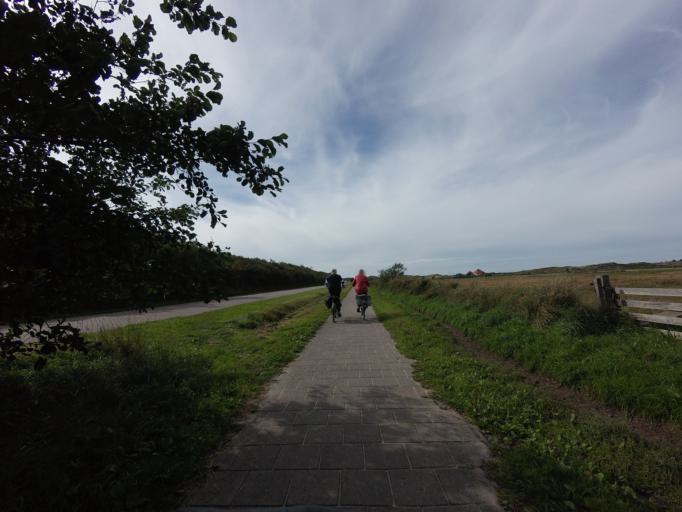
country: NL
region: North Holland
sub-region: Gemeente Texel
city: Den Burg
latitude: 53.0769
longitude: 4.7536
